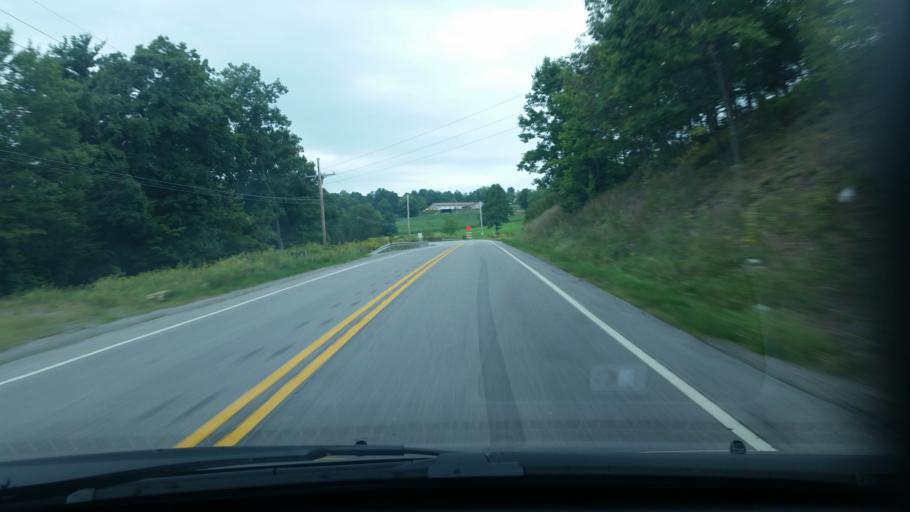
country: US
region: Pennsylvania
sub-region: Clearfield County
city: Shiloh
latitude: 41.0755
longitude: -78.3483
